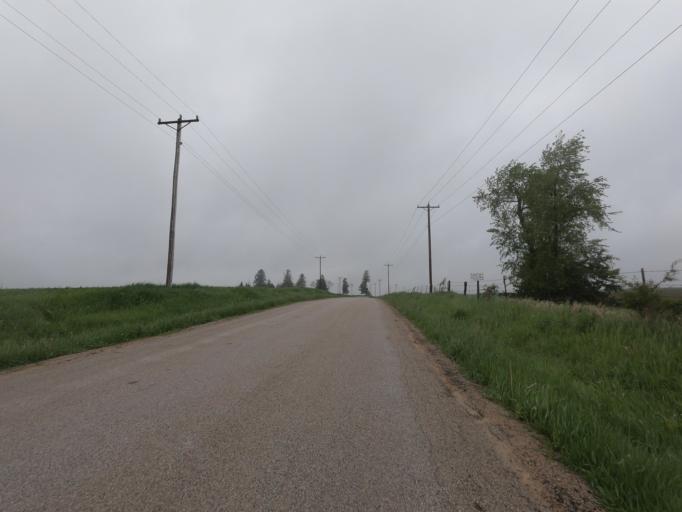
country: US
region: Wisconsin
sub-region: Grant County
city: Hazel Green
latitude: 42.5076
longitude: -90.5070
